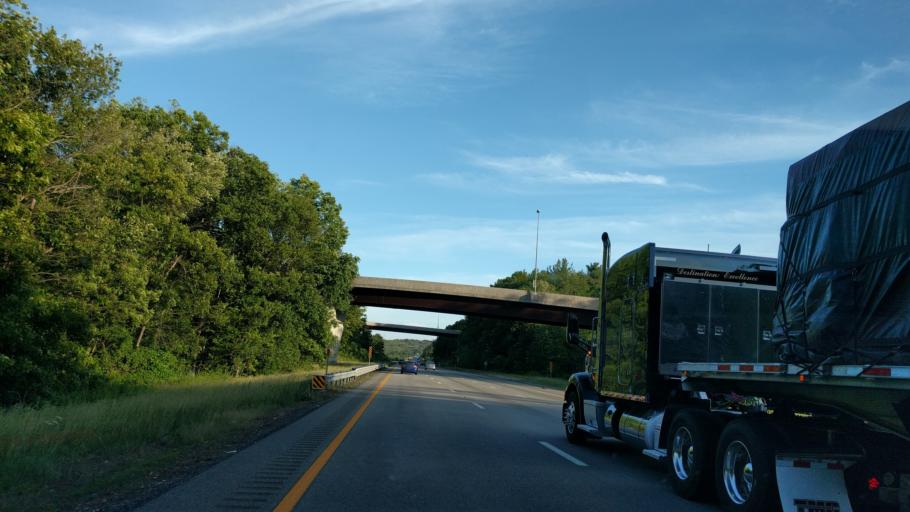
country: US
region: Massachusetts
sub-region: Middlesex County
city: Marlborough
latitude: 42.3233
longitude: -71.5725
